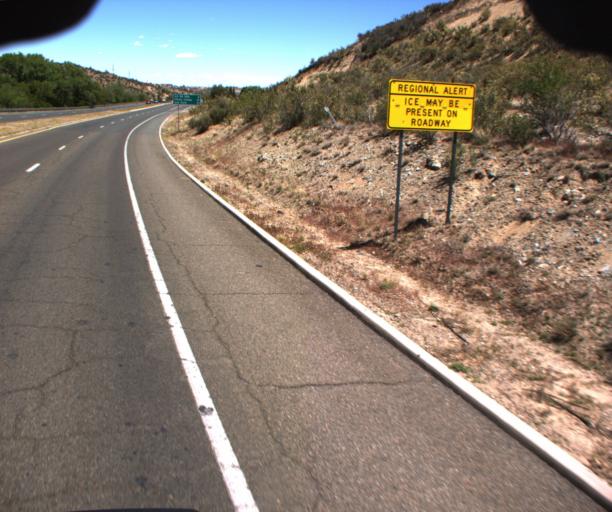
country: US
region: Arizona
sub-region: Yavapai County
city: Prescott
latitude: 34.5535
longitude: -112.4498
